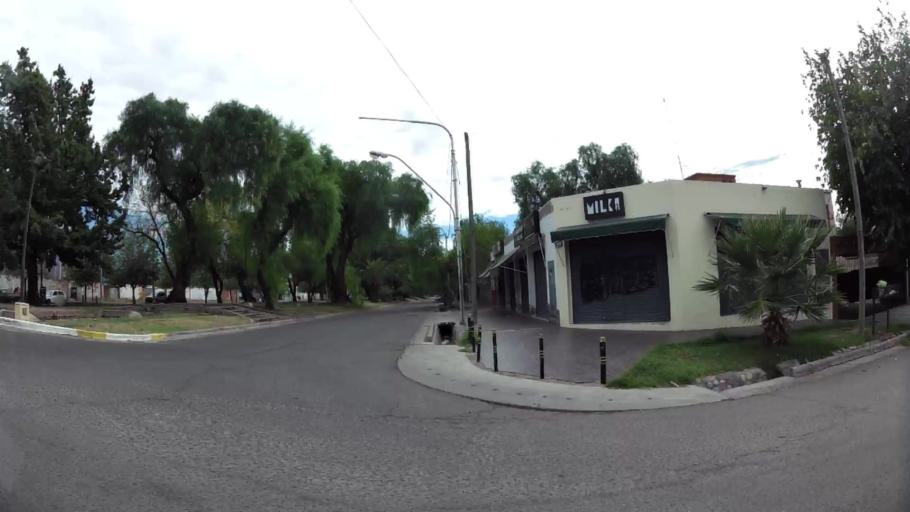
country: AR
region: Mendoza
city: Las Heras
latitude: -32.8617
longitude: -68.8584
